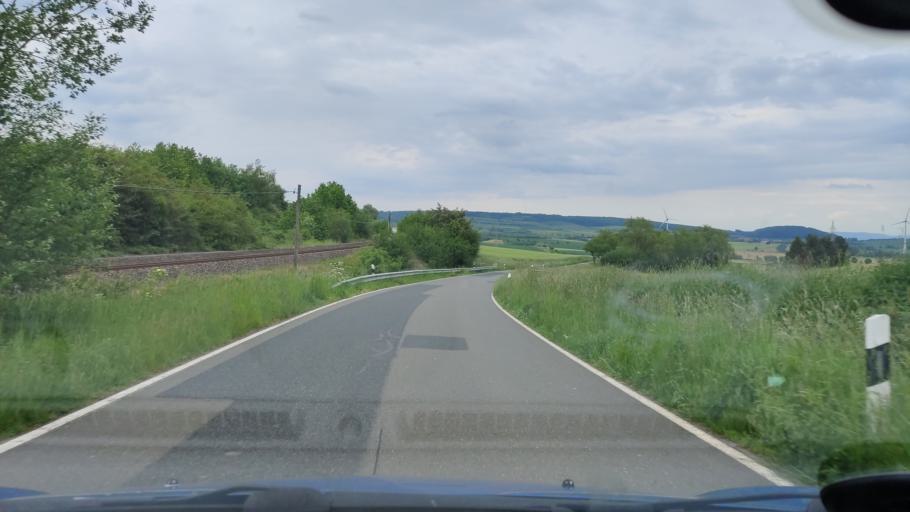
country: DE
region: Lower Saxony
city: Eimen
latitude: 51.8780
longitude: 9.8312
